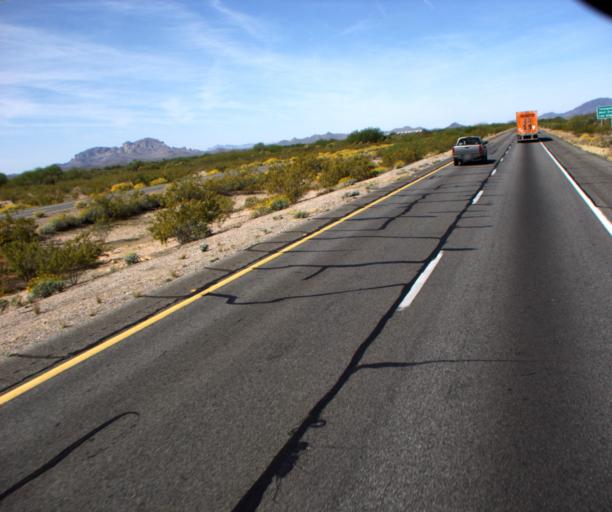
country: US
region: Arizona
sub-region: Maricopa County
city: Buckeye
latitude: 33.4856
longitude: -112.8834
